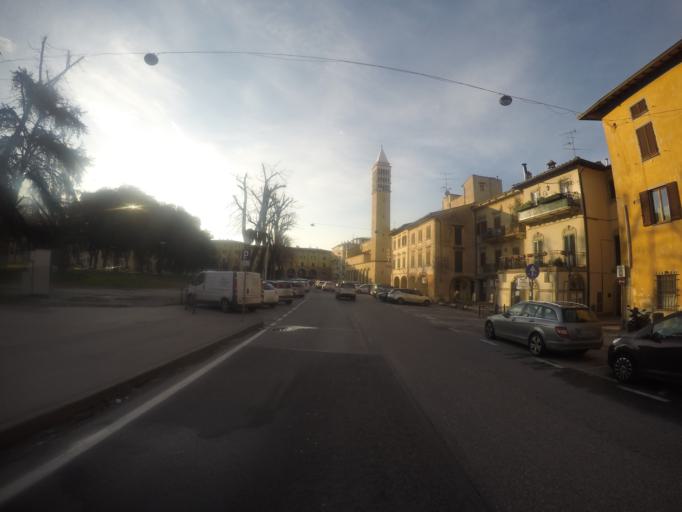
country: IT
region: Tuscany
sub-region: Provincia di Prato
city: Prato
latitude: 43.8804
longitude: 11.1012
